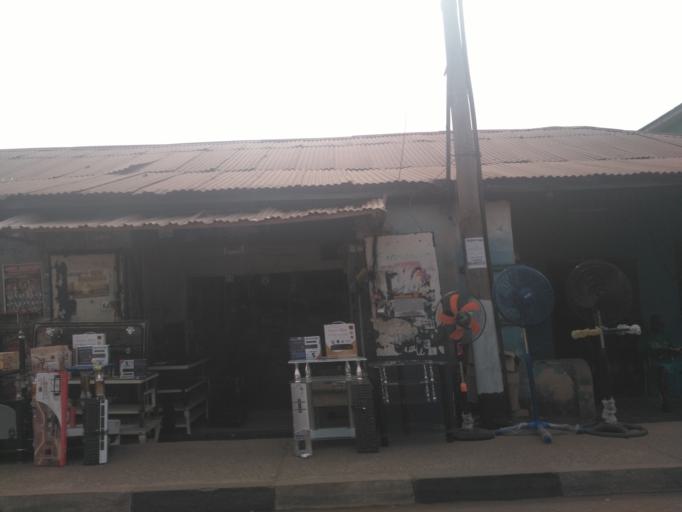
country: GH
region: Ashanti
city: Kumasi
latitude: 6.7029
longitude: -1.6331
